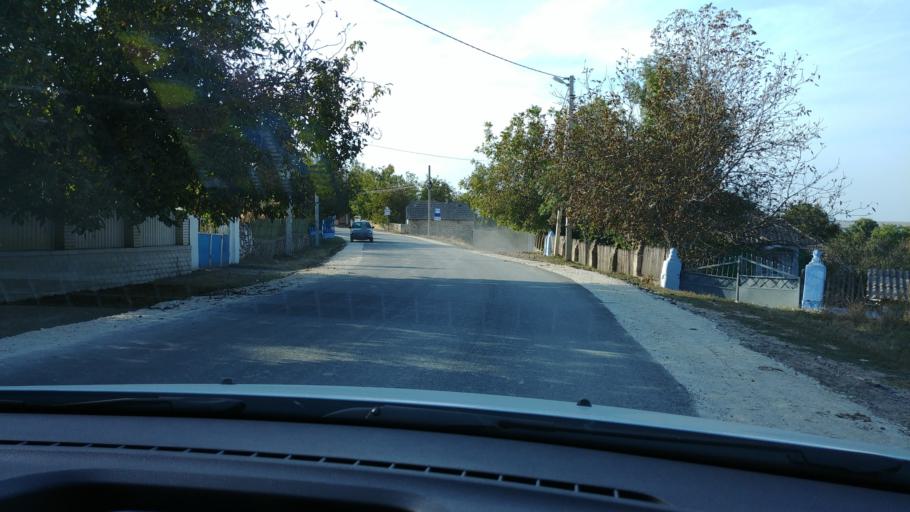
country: MD
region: Rezina
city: Rezina
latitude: 47.7488
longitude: 28.8842
